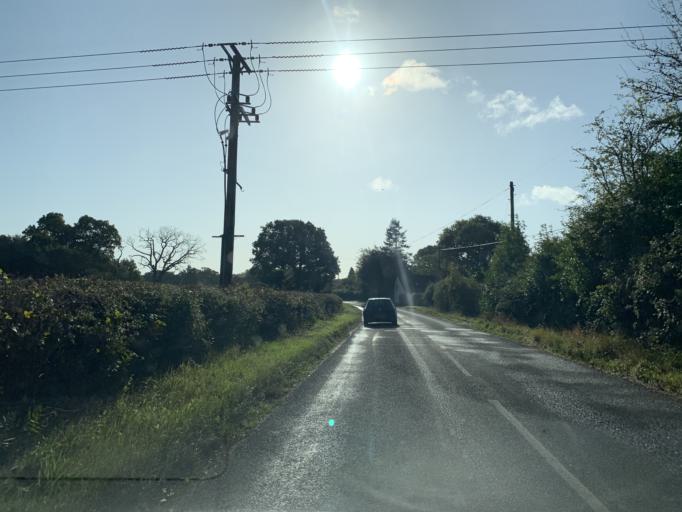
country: GB
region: England
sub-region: Wiltshire
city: Downton
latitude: 50.9748
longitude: -1.7175
